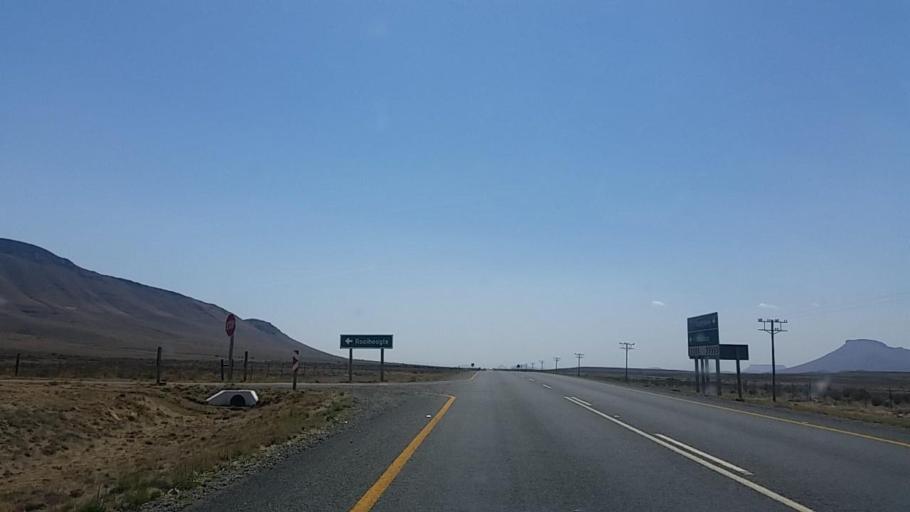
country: ZA
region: Eastern Cape
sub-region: Chris Hani District Municipality
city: Middelburg
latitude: -31.7631
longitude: 24.9196
